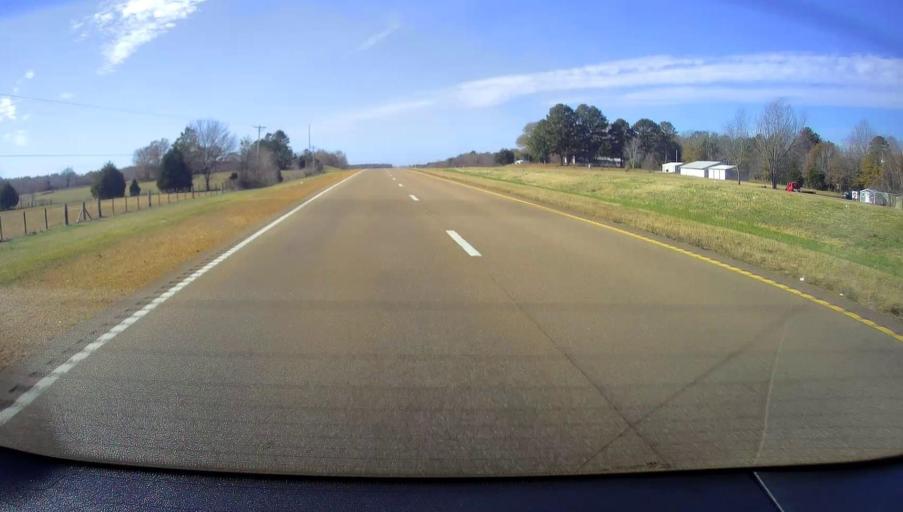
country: US
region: Mississippi
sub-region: Benton County
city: Ashland
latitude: 34.9456
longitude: -89.1447
